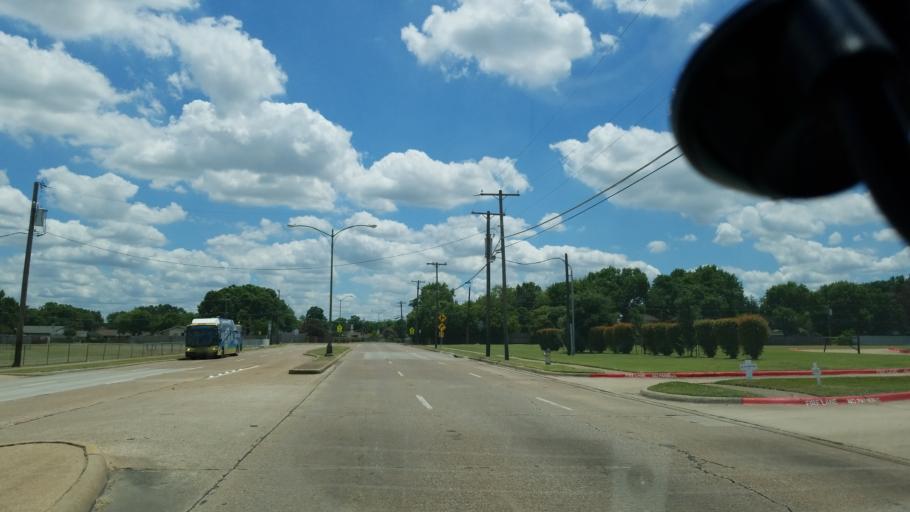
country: US
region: Texas
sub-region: Dallas County
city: Cockrell Hill
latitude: 32.6976
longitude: -96.8786
